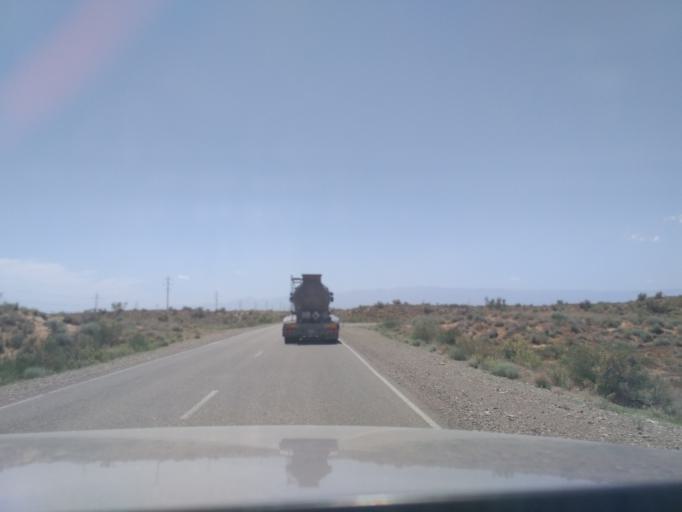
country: KZ
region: Ongtustik Qazaqstan
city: Sholaqqkorghan
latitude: 44.1345
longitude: 68.8919
